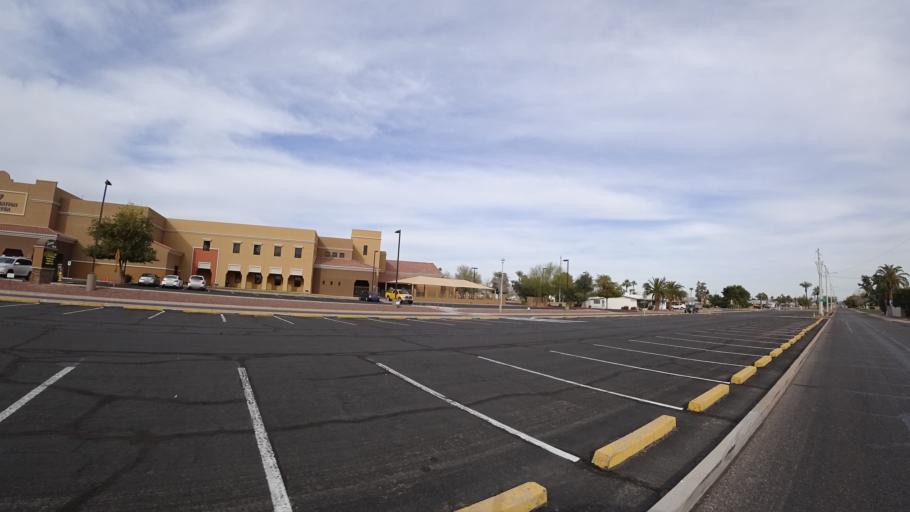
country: US
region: Arizona
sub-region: Maricopa County
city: Youngtown
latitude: 33.5801
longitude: -112.2882
